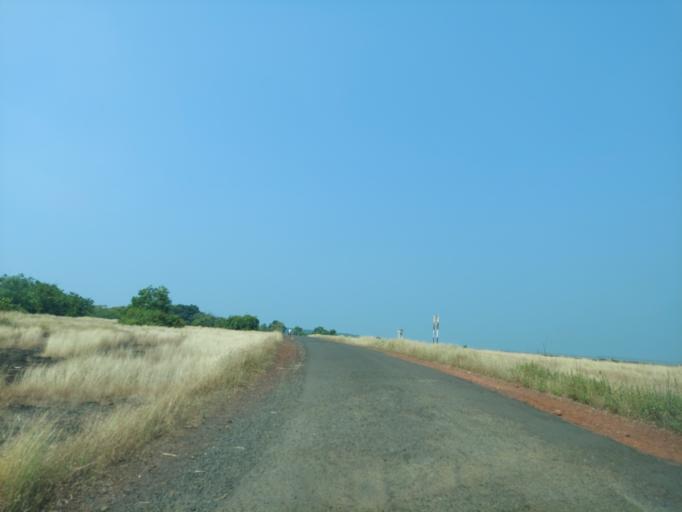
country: IN
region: Maharashtra
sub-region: Sindhudurg
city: Malvan
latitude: 15.9975
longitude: 73.5173
